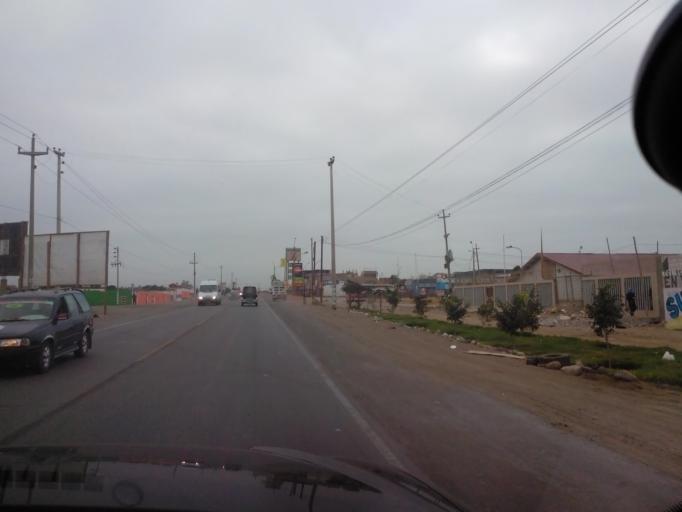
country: PE
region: Ica
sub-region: Provincia de Pisco
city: Villa Tupac Amaru
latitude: -13.7080
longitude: -76.1519
